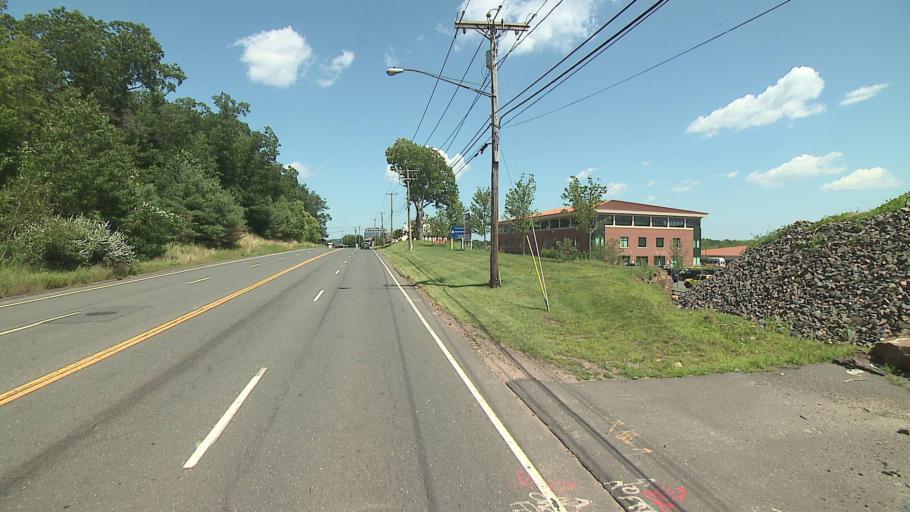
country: US
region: Connecticut
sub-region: Hartford County
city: Farmington
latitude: 41.7250
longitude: -72.8066
